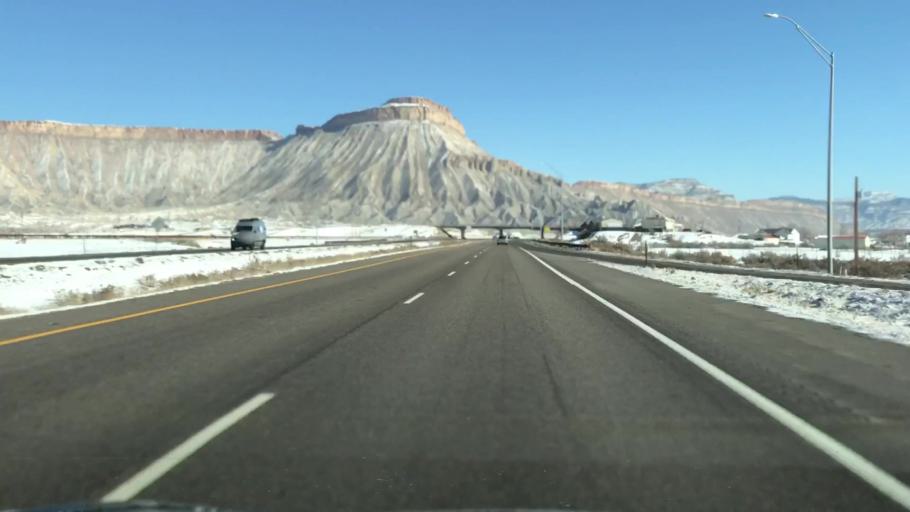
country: US
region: Colorado
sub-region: Mesa County
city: Clifton
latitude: 39.1048
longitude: -108.4455
